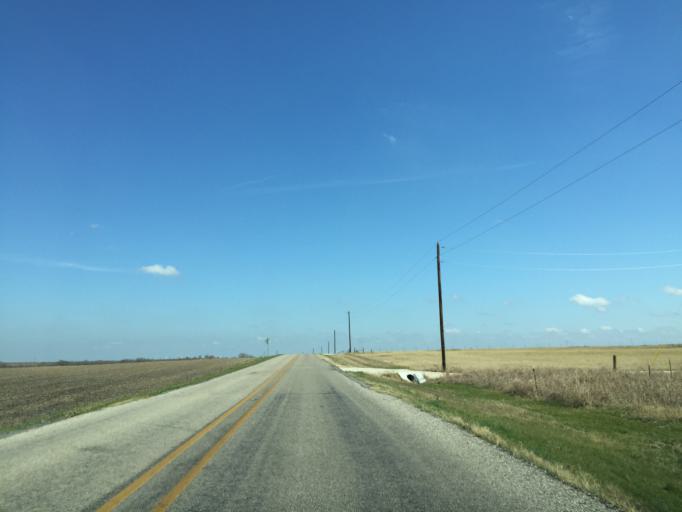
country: US
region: Texas
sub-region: Williamson County
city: Granger
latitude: 30.7533
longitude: -97.5173
